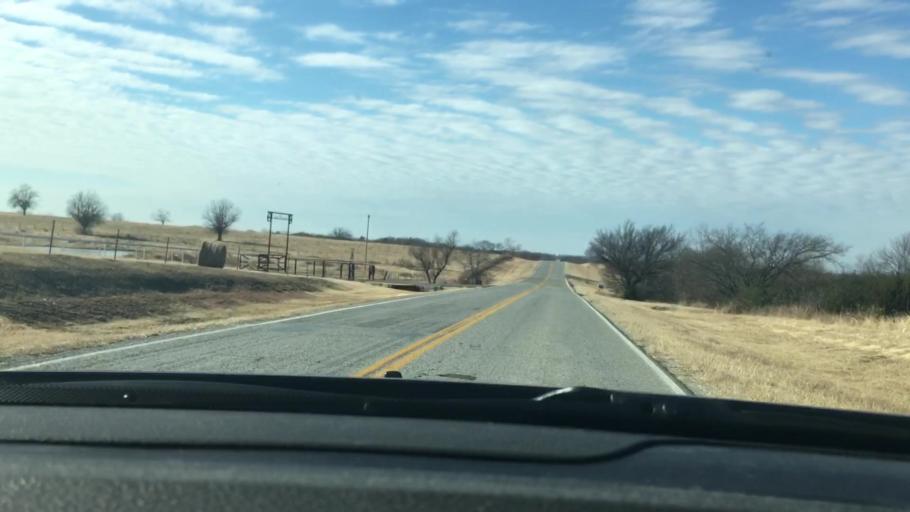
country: US
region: Oklahoma
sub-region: Garvin County
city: Wynnewood
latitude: 34.6515
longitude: -97.1056
